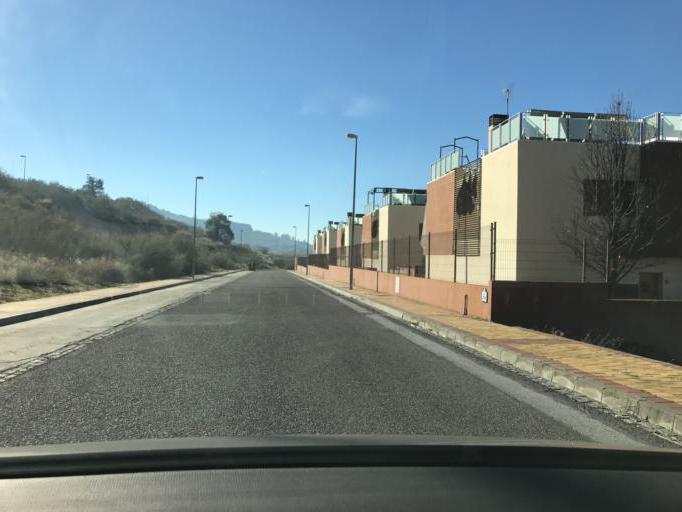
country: ES
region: Andalusia
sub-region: Provincia de Granada
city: Jun
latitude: 37.2115
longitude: -3.5914
